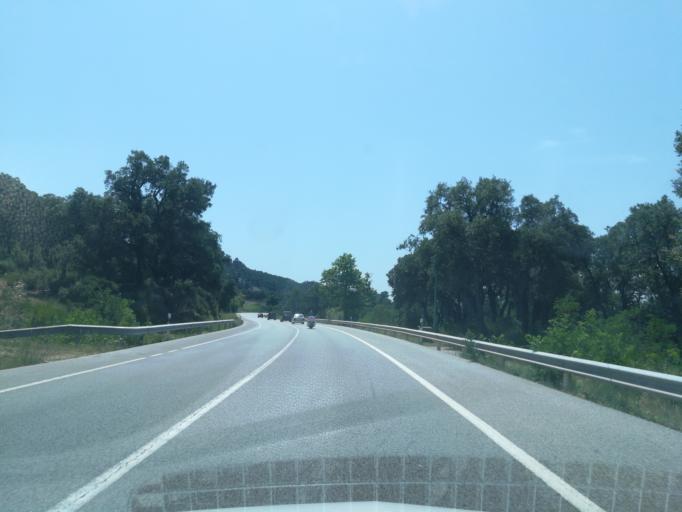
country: ES
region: Catalonia
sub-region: Provincia de Girona
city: la Jonquera
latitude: 42.4479
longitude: 2.8659
